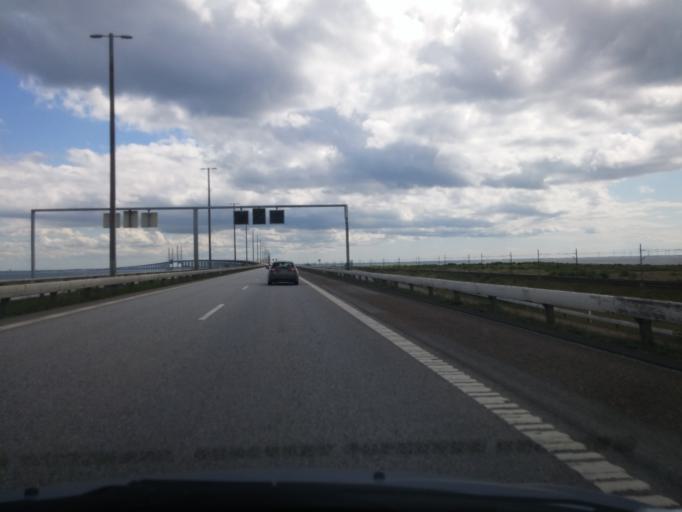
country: DK
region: Capital Region
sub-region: Dragor Kommune
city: Dragor
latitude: 55.5996
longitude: 12.7524
